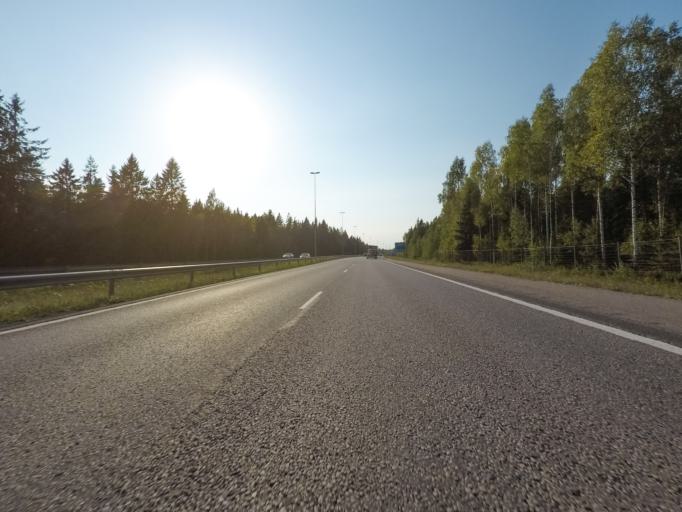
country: FI
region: Uusimaa
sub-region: Helsinki
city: Kirkkonummi
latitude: 60.2667
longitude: 24.4787
